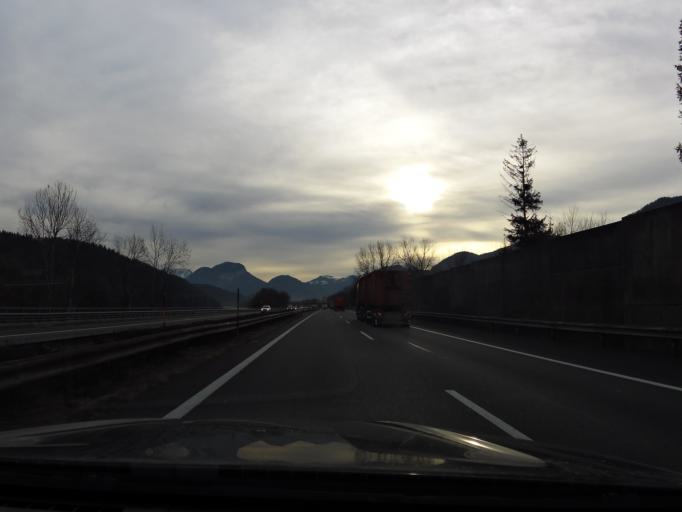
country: AT
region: Tyrol
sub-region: Politischer Bezirk Kufstein
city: Kundl
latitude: 47.4798
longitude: 11.9894
